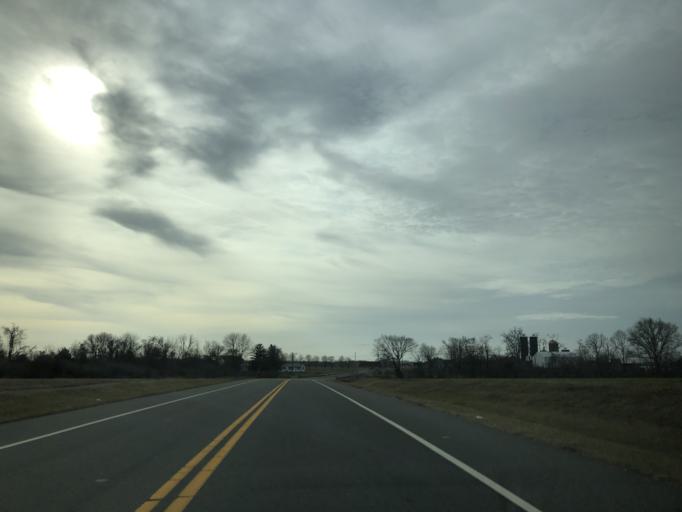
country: US
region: Delaware
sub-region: New Castle County
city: Middletown
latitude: 39.5164
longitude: -75.6788
